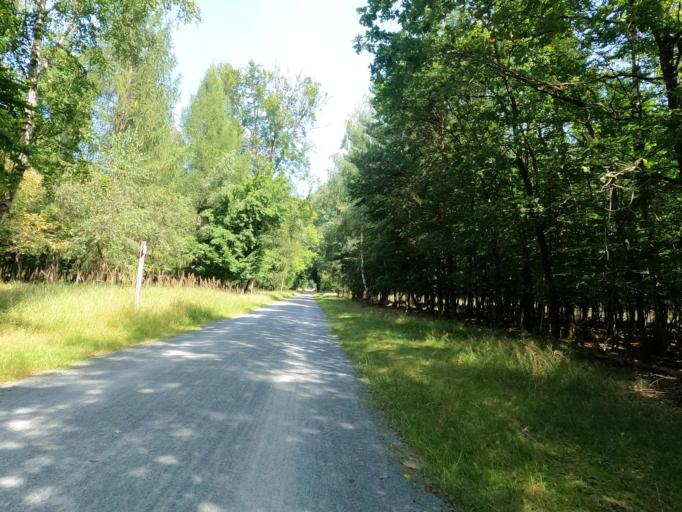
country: DE
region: Hesse
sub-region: Regierungsbezirk Darmstadt
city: Neu Isenburg
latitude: 50.0662
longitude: 8.7103
